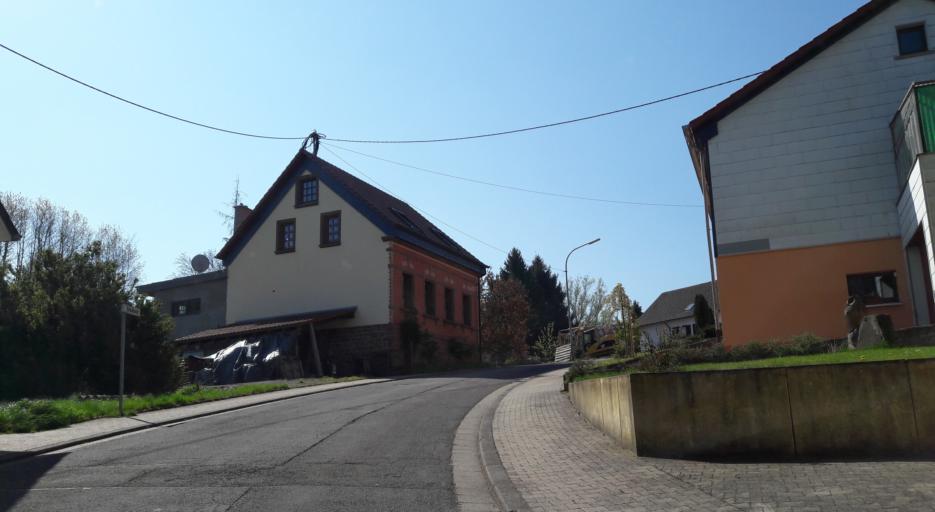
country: DE
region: Saarland
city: Schiffweiler
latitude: 49.3680
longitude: 7.1159
